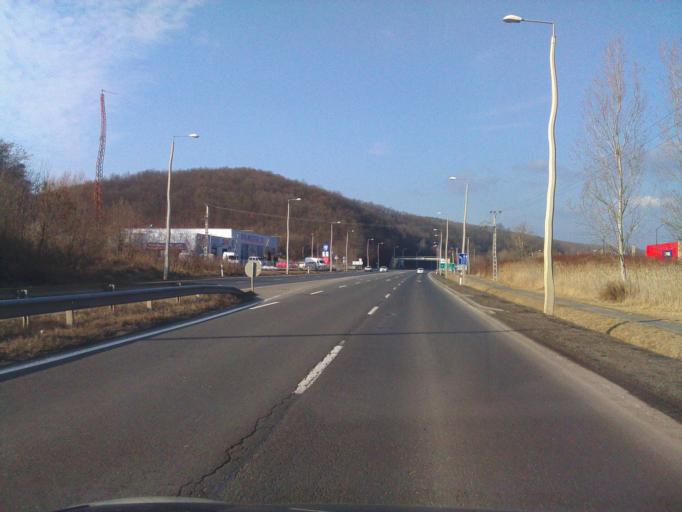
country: HU
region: Nograd
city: Salgotarjan
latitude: 48.0510
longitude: 19.7815
